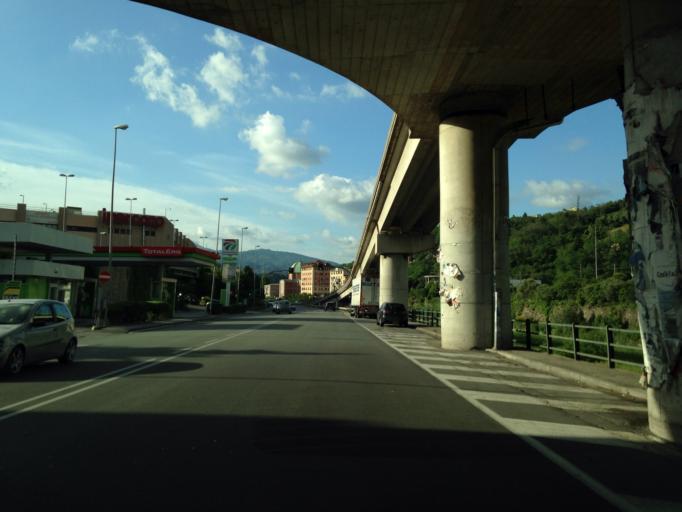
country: IT
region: Liguria
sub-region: Provincia di Genova
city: Manesseno
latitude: 44.4699
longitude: 8.9013
